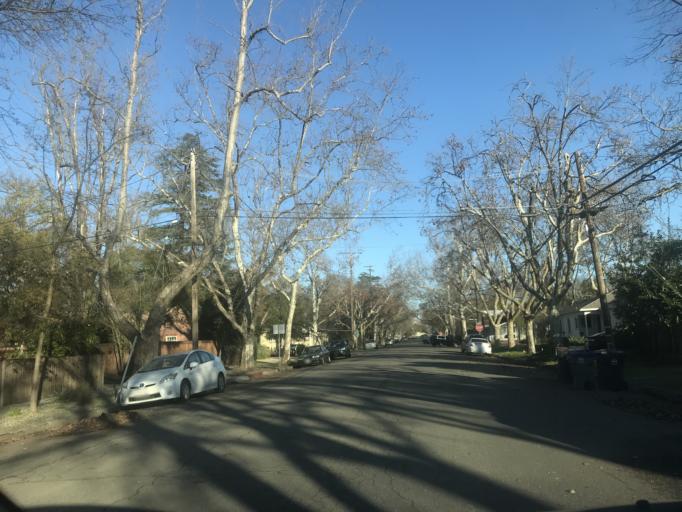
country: US
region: California
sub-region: Yolo County
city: Davis
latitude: 38.5480
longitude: -121.7445
